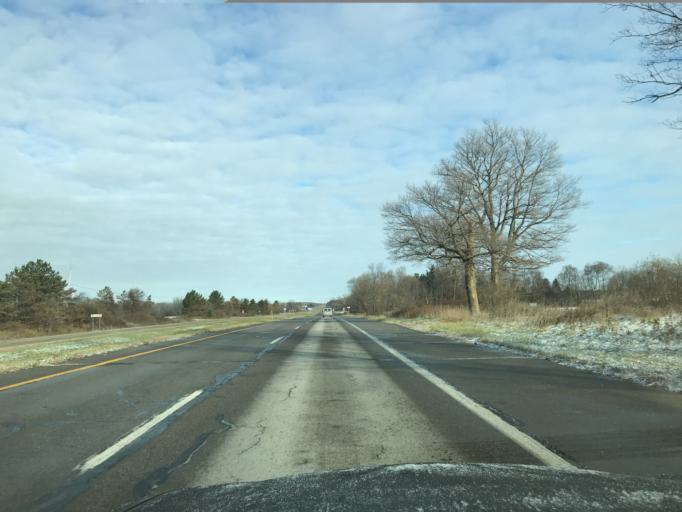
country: US
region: Michigan
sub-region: Eaton County
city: Dimondale
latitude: 42.6052
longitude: -84.6222
